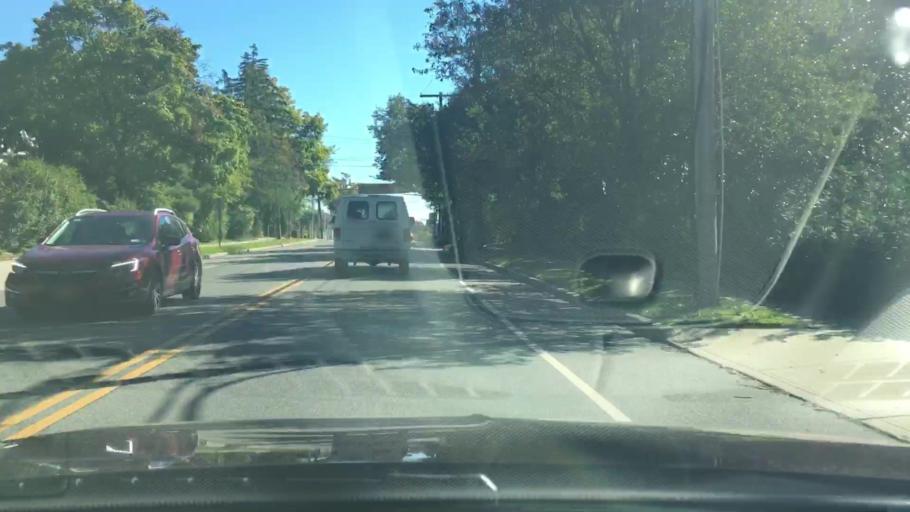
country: US
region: New York
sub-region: Nassau County
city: Plandome Heights
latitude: 40.8011
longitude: -73.7027
